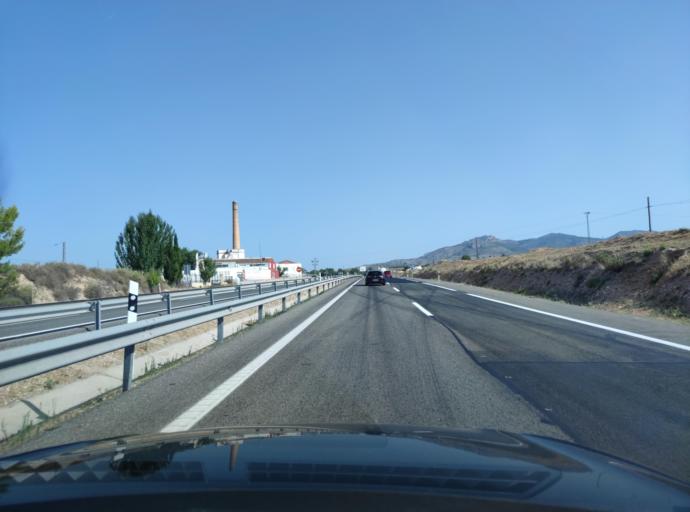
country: ES
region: Valencia
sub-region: Provincia de Alicante
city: Sax
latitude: 38.5438
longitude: -0.8125
